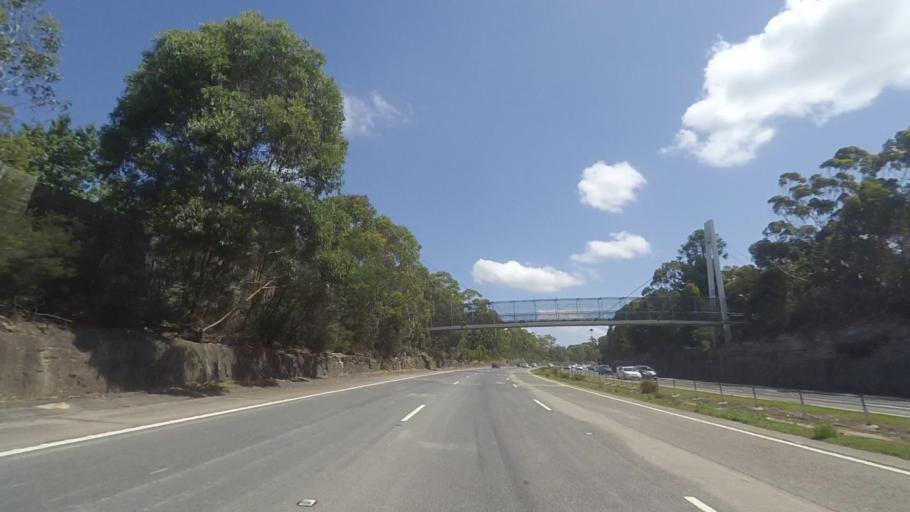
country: AU
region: New South Wales
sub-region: Hornsby Shire
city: Berowra
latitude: -33.6535
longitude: 151.1376
